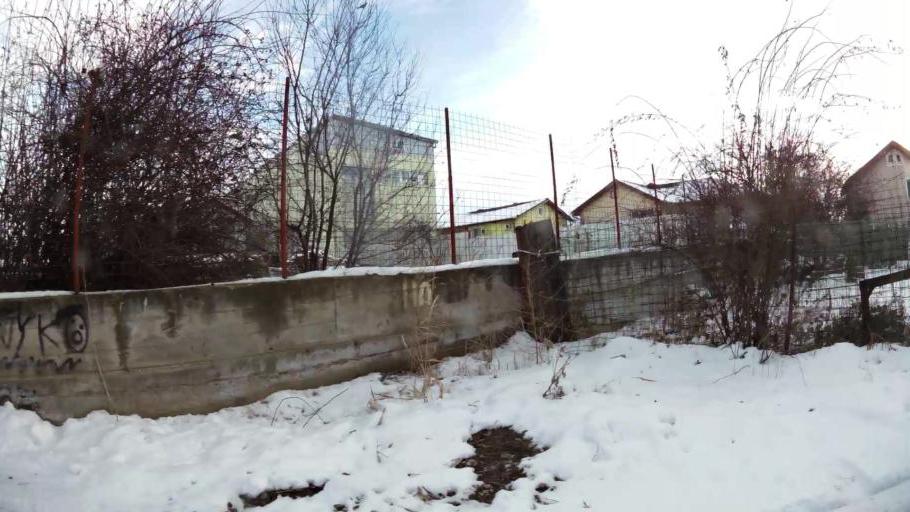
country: RO
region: Ilfov
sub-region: Comuna Fundeni-Dobroesti
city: Fundeni
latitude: 44.4633
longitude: 26.1673
